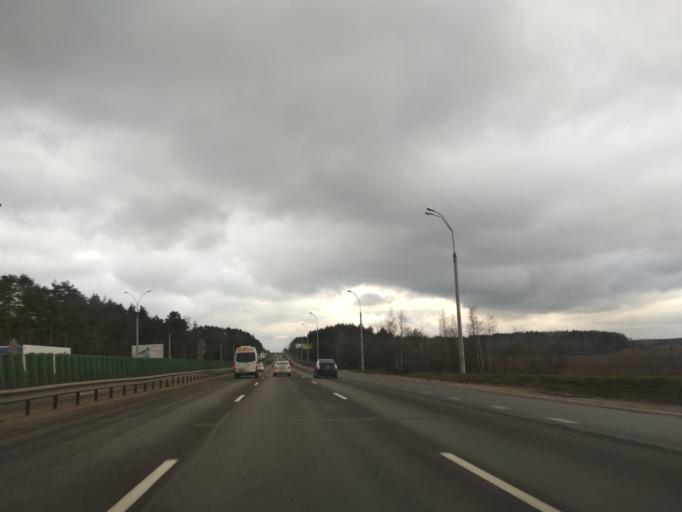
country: BY
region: Minsk
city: Vyaliki Trastsyanets
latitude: 53.8329
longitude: 27.7367
